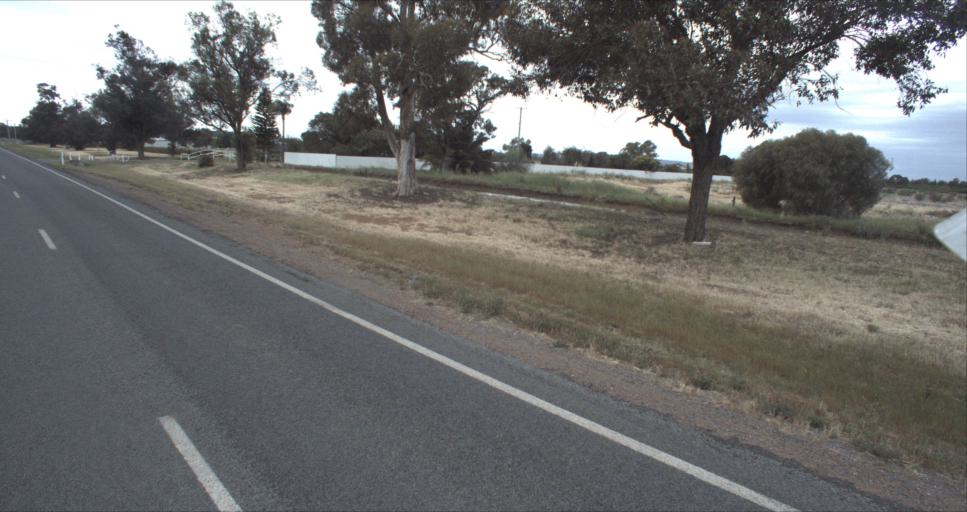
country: AU
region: New South Wales
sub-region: Leeton
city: Leeton
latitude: -34.5411
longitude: 146.3869
